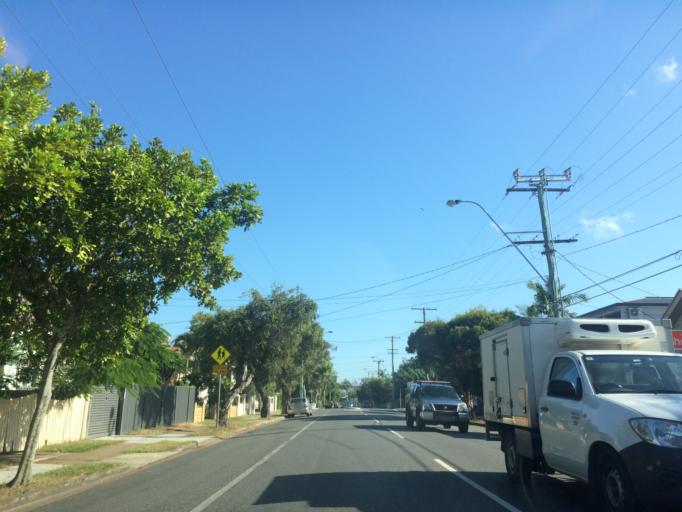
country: AU
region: Queensland
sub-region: Brisbane
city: Balmoral
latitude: -27.4603
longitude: 153.0607
